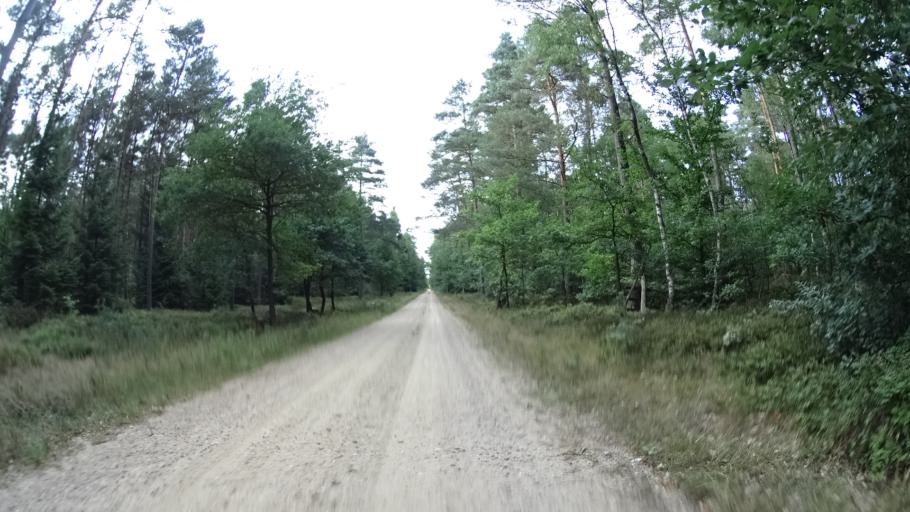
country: DE
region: Lower Saxony
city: Handeloh
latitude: 53.1840
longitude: 9.8843
